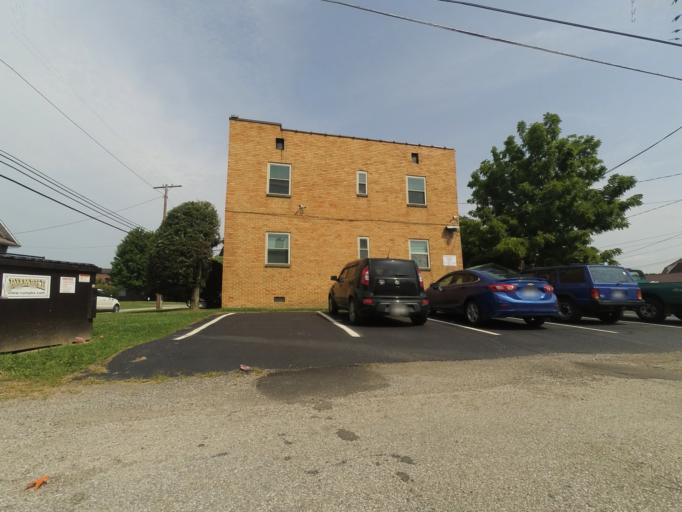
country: US
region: West Virginia
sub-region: Cabell County
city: Huntington
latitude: 38.4126
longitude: -82.4641
